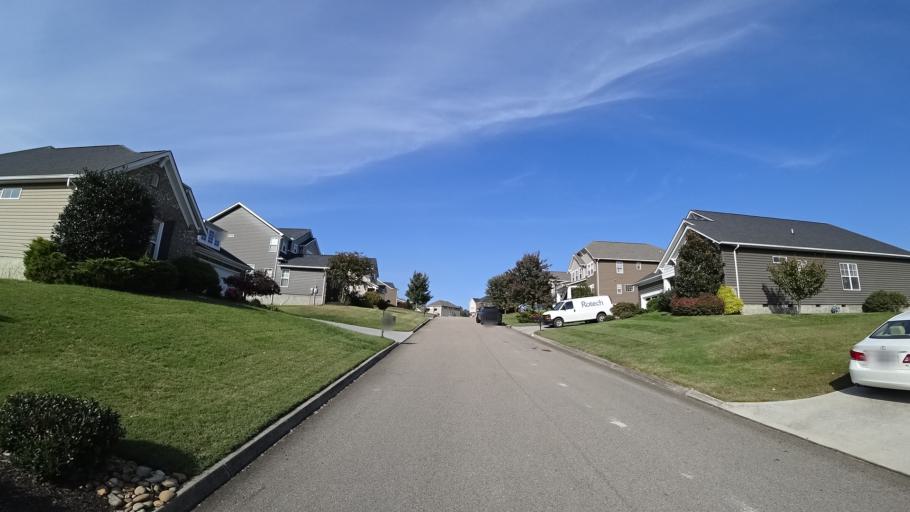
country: US
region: Tennessee
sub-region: Knox County
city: Farragut
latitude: 35.9192
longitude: -84.1539
